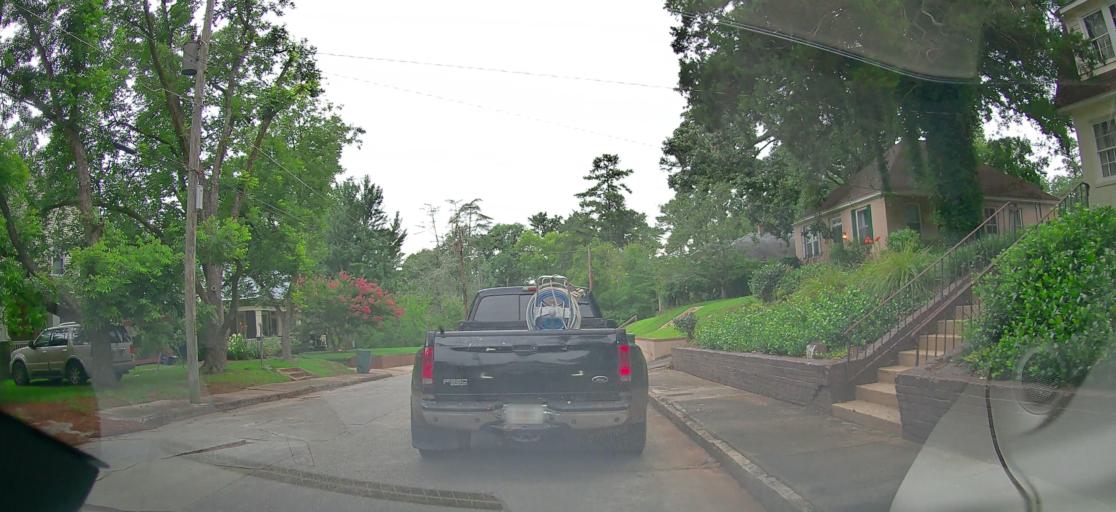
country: US
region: Georgia
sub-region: Bibb County
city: Macon
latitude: 32.8563
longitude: -83.6266
